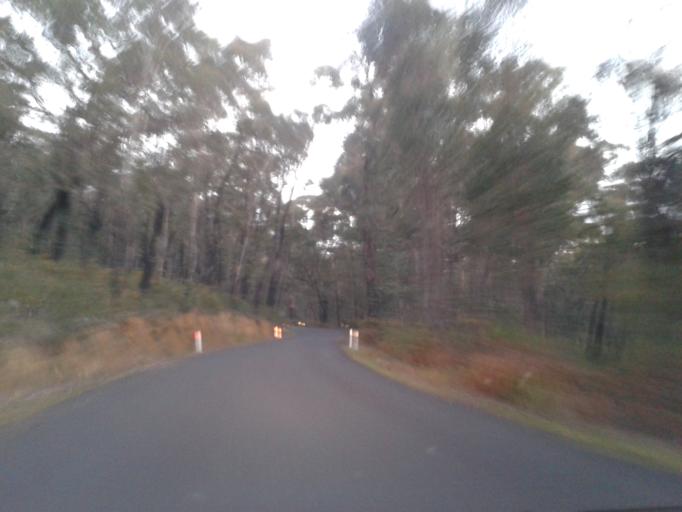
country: AU
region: Victoria
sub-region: Northern Grampians
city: Stawell
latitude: -37.1650
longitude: 142.4963
